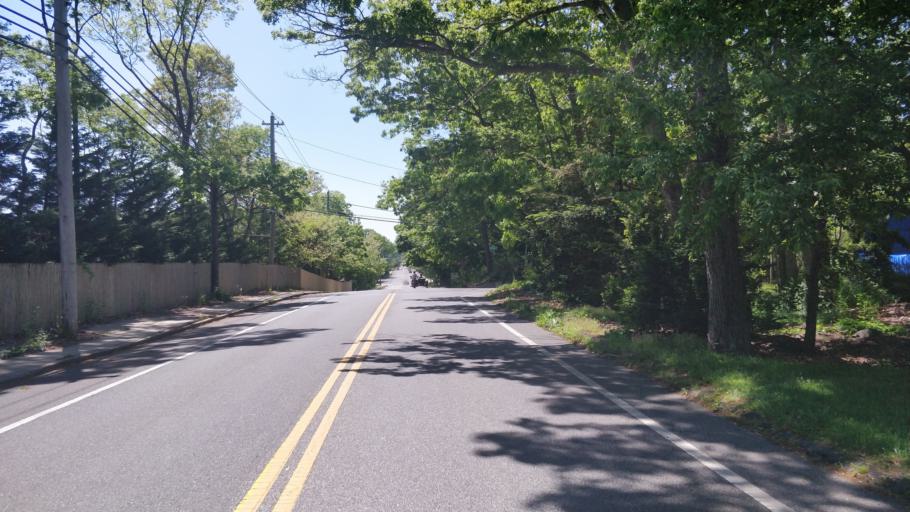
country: US
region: New York
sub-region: Suffolk County
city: Islandia
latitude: 40.8279
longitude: -73.1649
